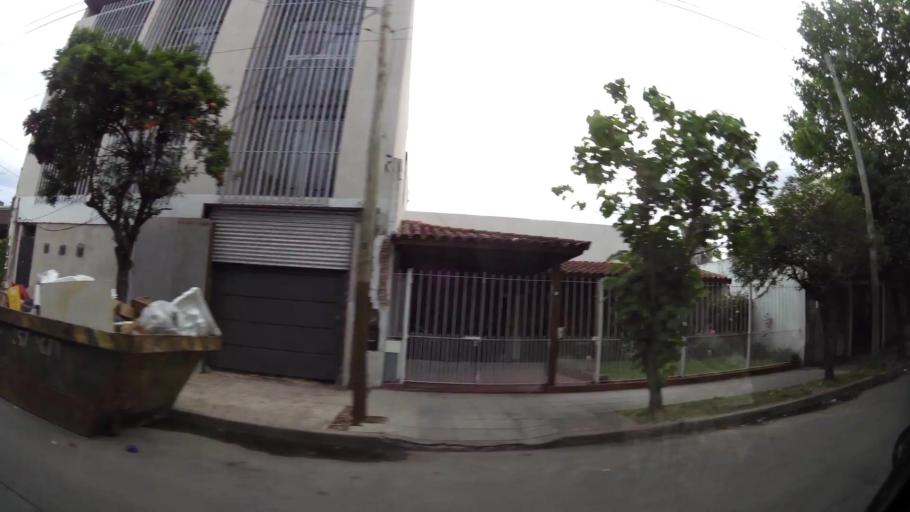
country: AR
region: Buenos Aires
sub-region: Partido de Quilmes
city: Quilmes
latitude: -34.7312
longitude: -58.2508
